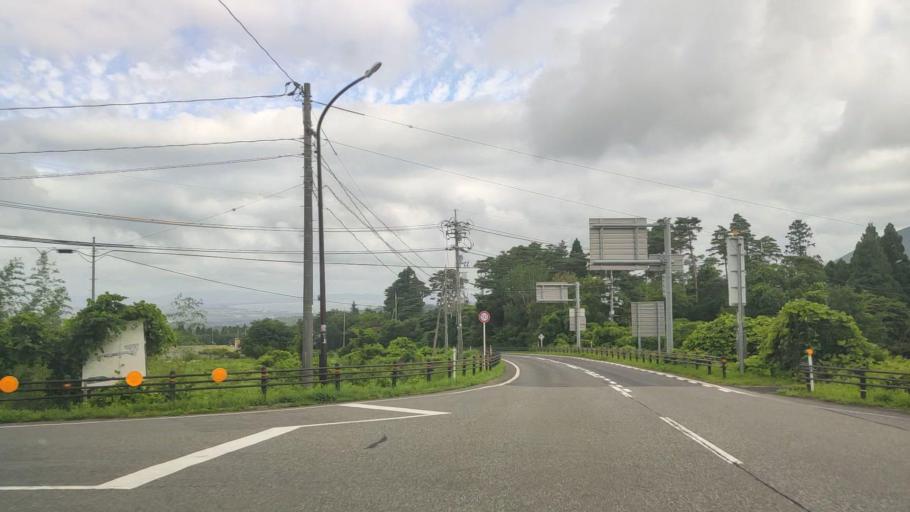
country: JP
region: Tottori
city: Yonago
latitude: 35.4084
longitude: 133.4798
